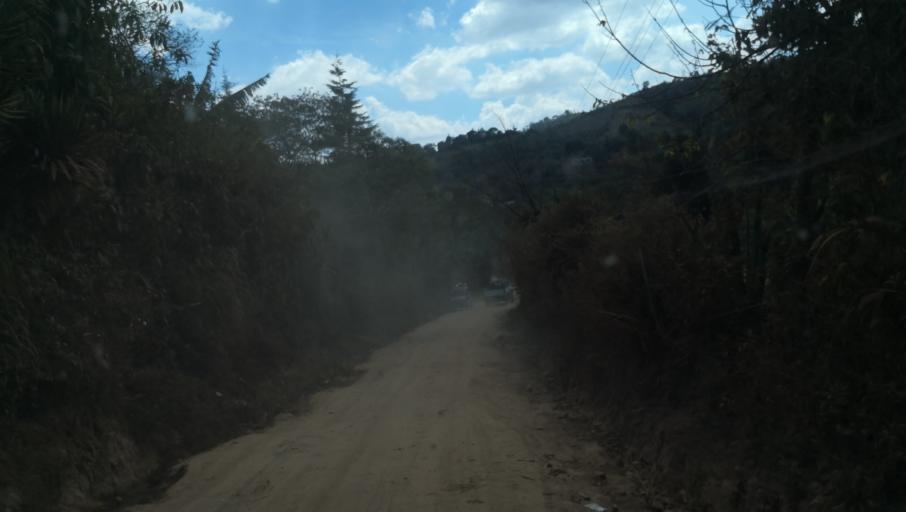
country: GT
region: Jalapa
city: San Carlos Alzatate
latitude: 14.3971
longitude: -89.9920
